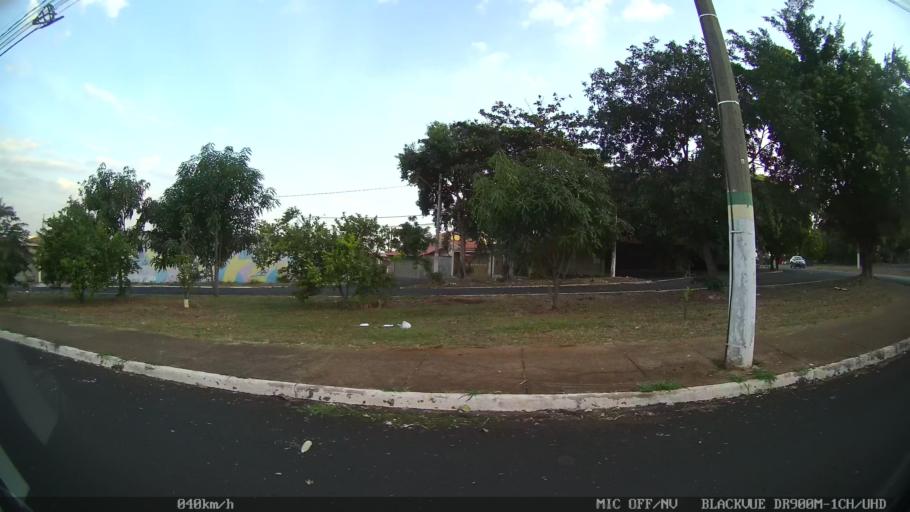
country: BR
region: Sao Paulo
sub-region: Ribeirao Preto
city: Ribeirao Preto
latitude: -21.1359
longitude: -47.8467
